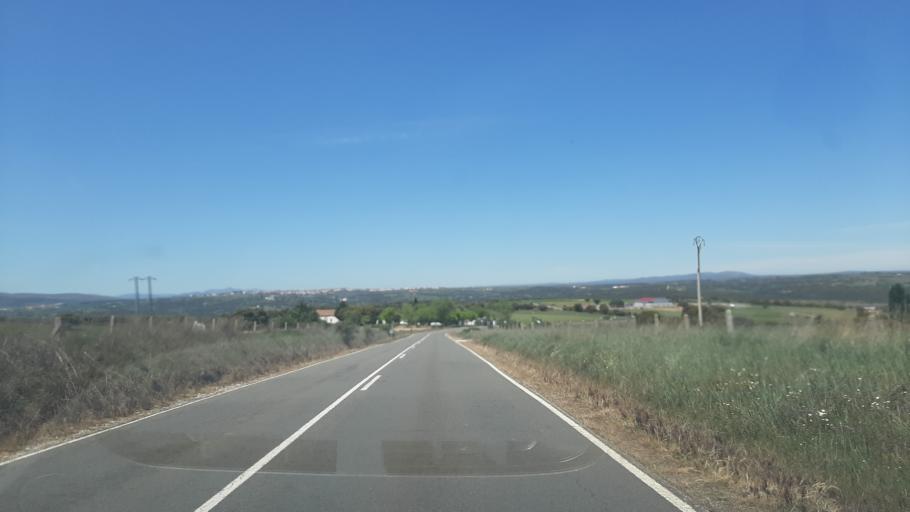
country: ES
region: Castille and Leon
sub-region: Provincia de Salamanca
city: Salvatierra de Tormes
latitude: 40.5439
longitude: -5.5915
